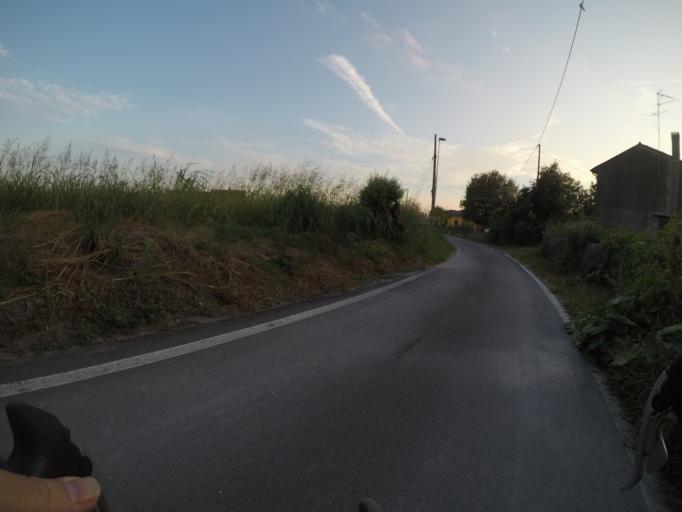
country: IT
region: Veneto
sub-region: Provincia di Rovigo
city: San Bellino
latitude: 45.0208
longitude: 11.5948
